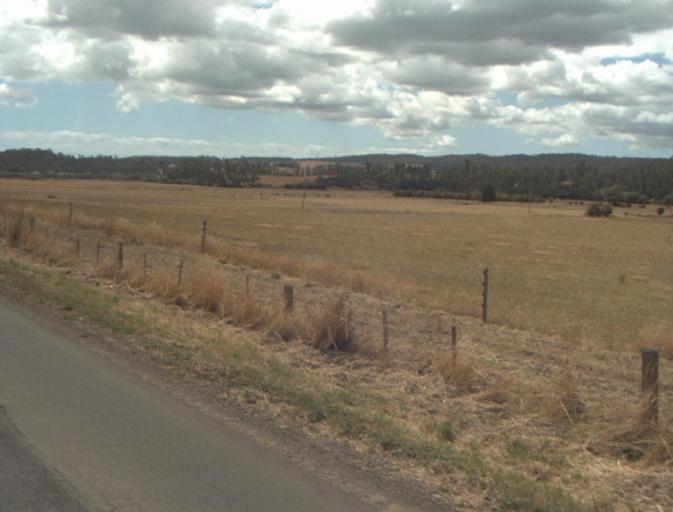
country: AU
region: Tasmania
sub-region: Launceston
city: Mayfield
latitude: -41.2434
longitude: 147.1393
